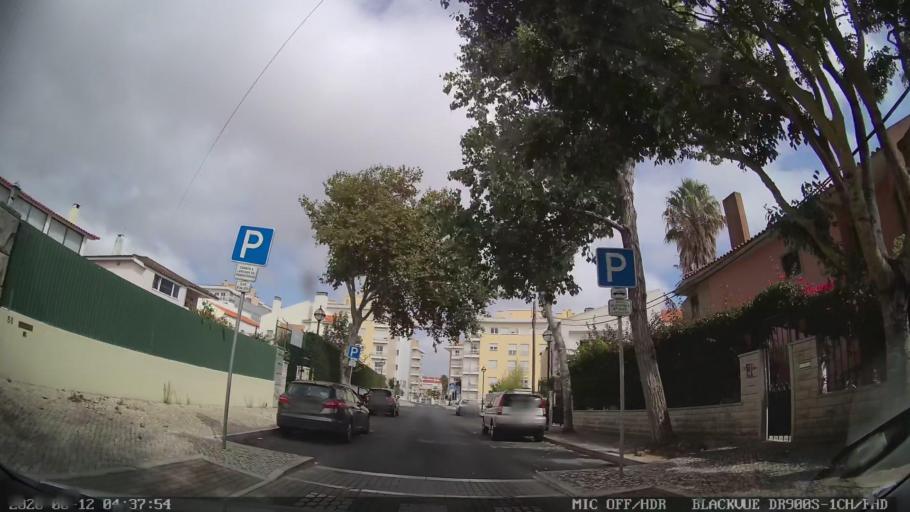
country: PT
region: Lisbon
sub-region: Cascais
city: Parede
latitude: 38.6956
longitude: -9.3695
